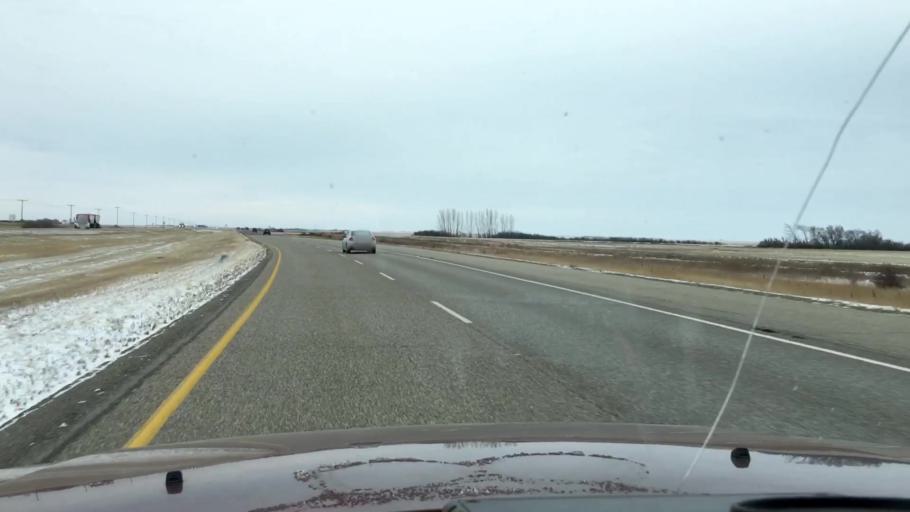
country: CA
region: Saskatchewan
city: Watrous
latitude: 51.1433
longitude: -105.9055
